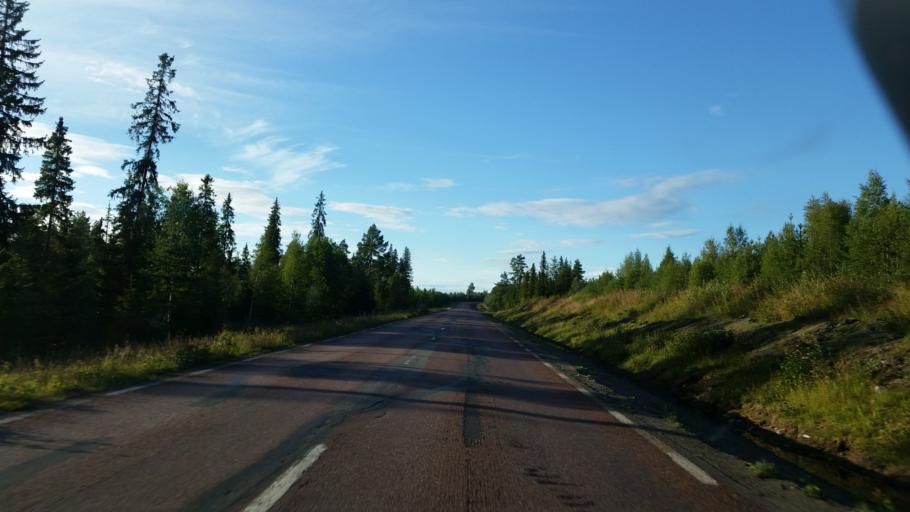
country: SE
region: Vaesterbotten
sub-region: Dorotea Kommun
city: Dorotea
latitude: 64.1348
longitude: 16.2240
